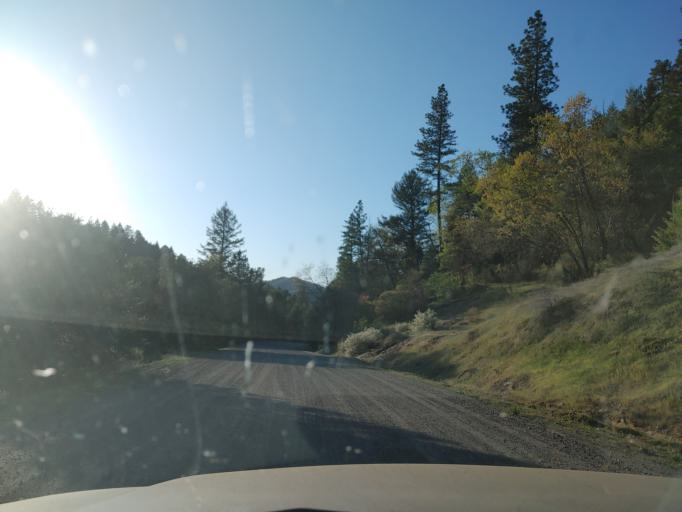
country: US
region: California
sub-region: Shasta County
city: Bella Vista
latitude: 40.8124
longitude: -122.0055
